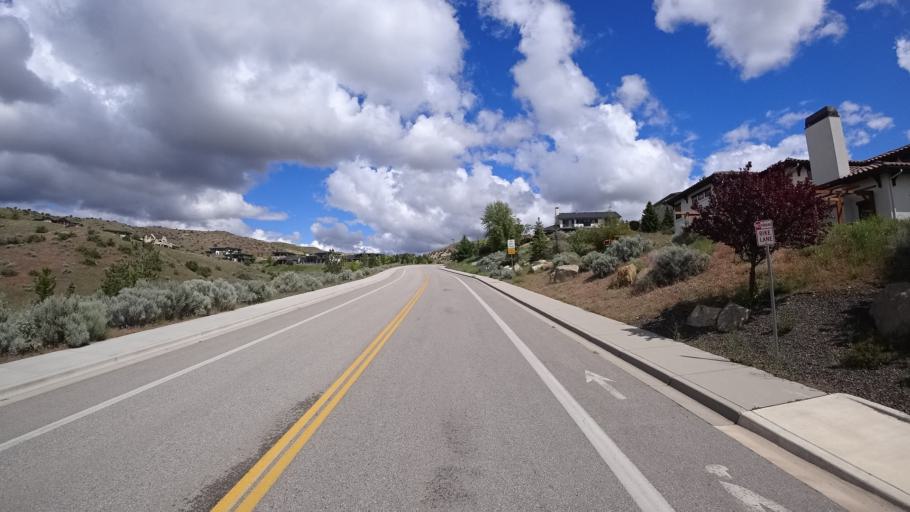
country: US
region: Idaho
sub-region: Ada County
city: Boise
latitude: 43.6583
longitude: -116.1896
